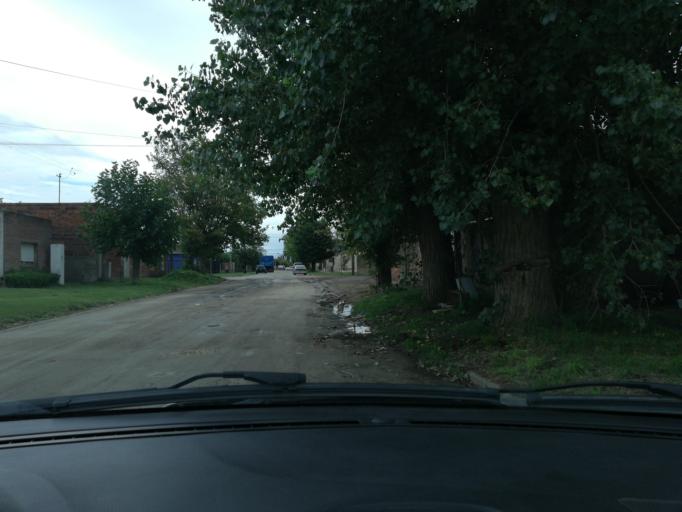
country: AR
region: Buenos Aires
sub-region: Partido de Balcarce
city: Balcarce
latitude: -37.8512
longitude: -58.2434
